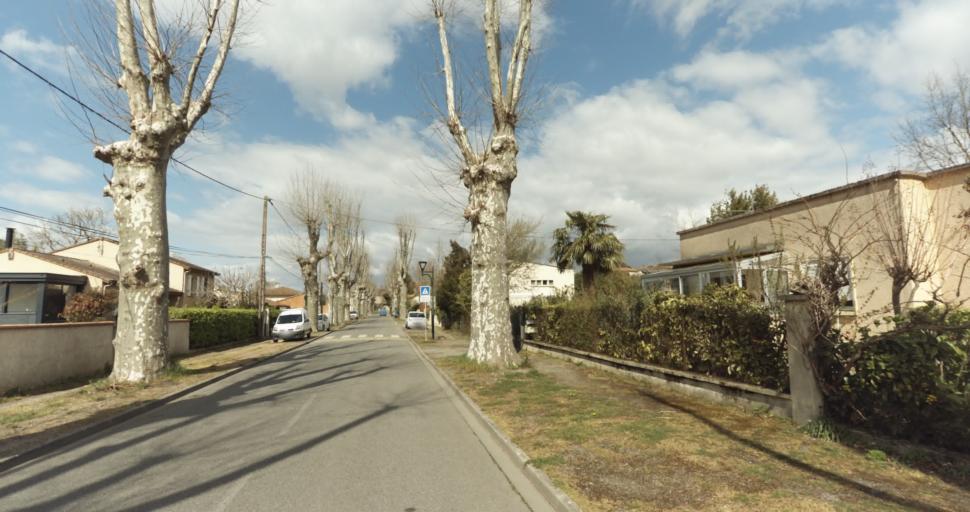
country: FR
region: Midi-Pyrenees
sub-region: Departement de la Haute-Garonne
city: Auterive
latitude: 43.3474
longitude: 1.4788
